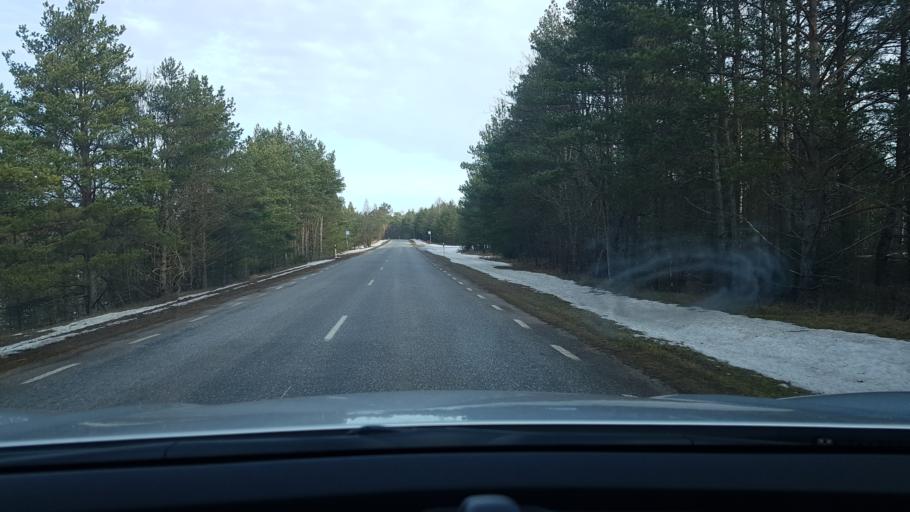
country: EE
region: Saare
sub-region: Kuressaare linn
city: Kuressaare
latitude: 58.4437
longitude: 22.7064
